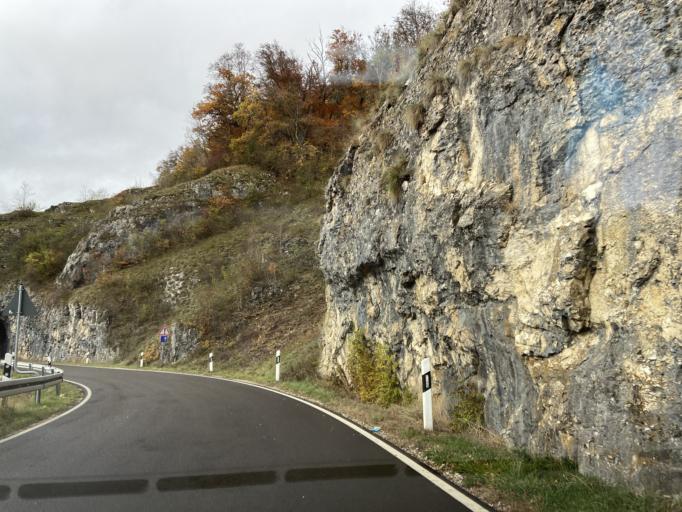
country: DE
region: Baden-Wuerttemberg
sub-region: Tuebingen Region
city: Stetten am Kalten Markt
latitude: 48.0810
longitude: 9.1145
